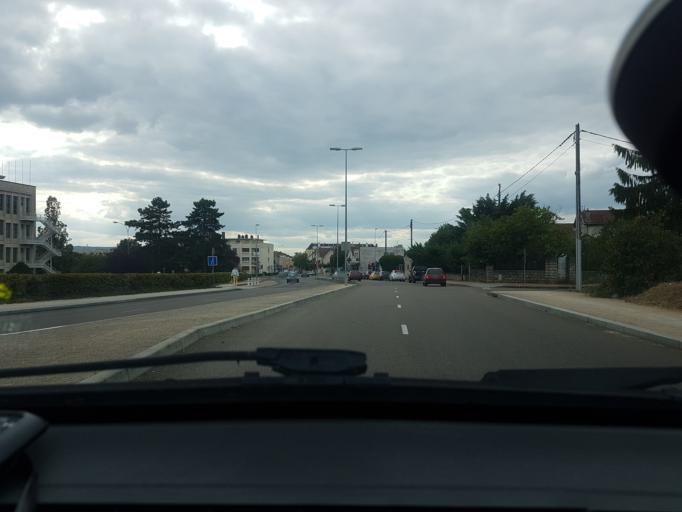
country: FR
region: Bourgogne
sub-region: Departement de la Cote-d'Or
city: Saint-Apollinaire
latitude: 47.3170
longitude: 5.0671
